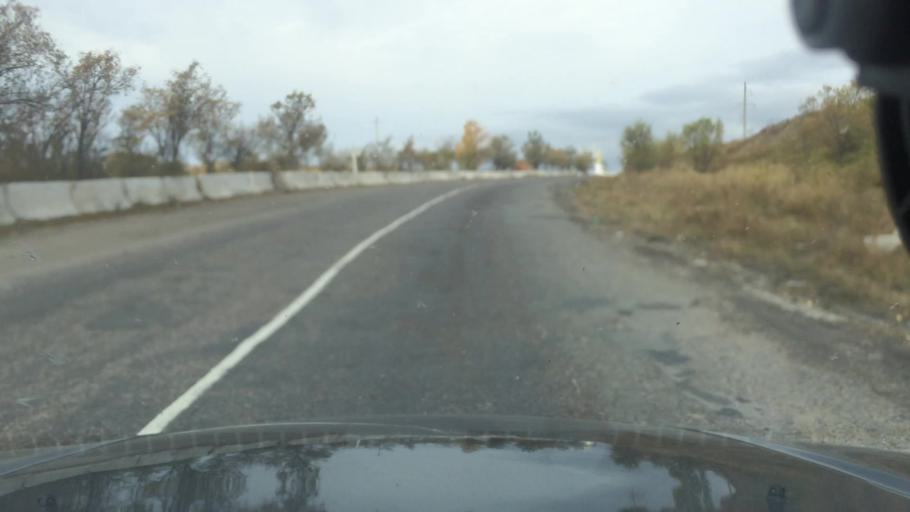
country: KG
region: Ysyk-Koel
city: Karakol
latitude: 42.5971
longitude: 78.3771
